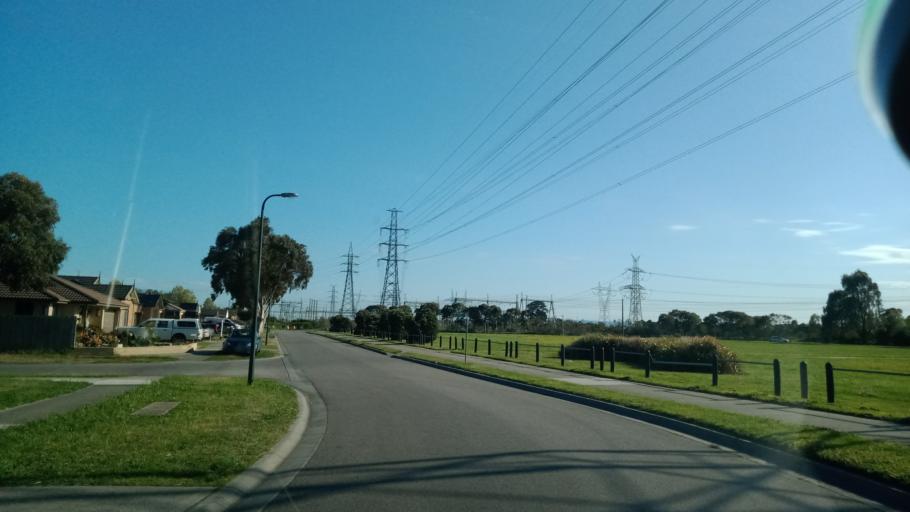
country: AU
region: Victoria
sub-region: Casey
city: Cranbourne West
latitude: -38.0901
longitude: 145.2655
